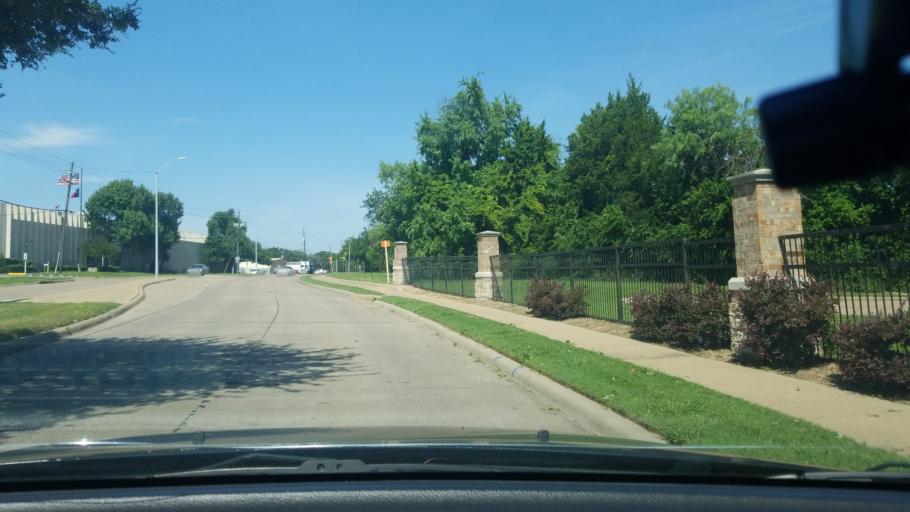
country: US
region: Texas
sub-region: Dallas County
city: Mesquite
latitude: 32.7703
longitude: -96.5871
